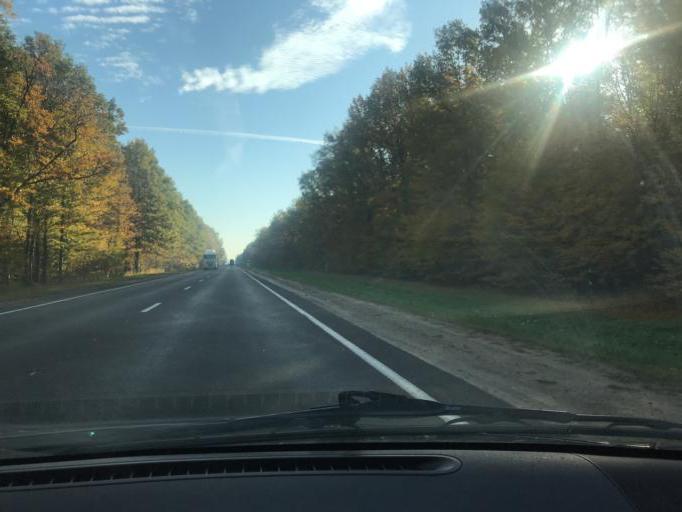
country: BY
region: Brest
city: Ivanava
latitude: 52.1535
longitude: 25.3547
